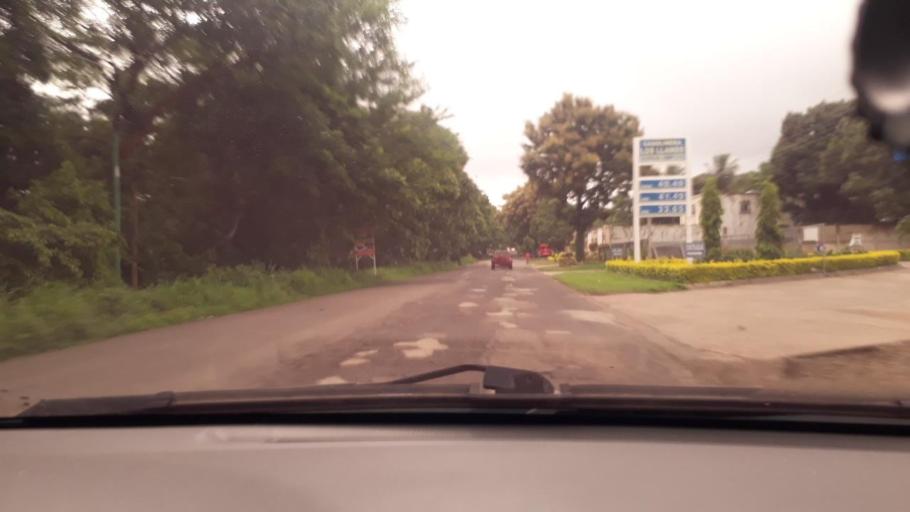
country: GT
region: Jutiapa
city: Jalpatagua
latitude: 14.1509
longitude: -90.0400
